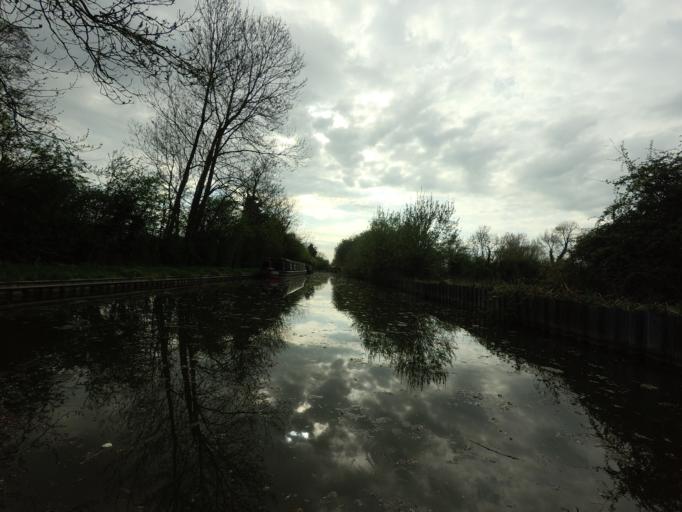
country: GB
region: England
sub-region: Buckinghamshire
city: Cheddington
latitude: 51.8206
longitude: -0.6916
